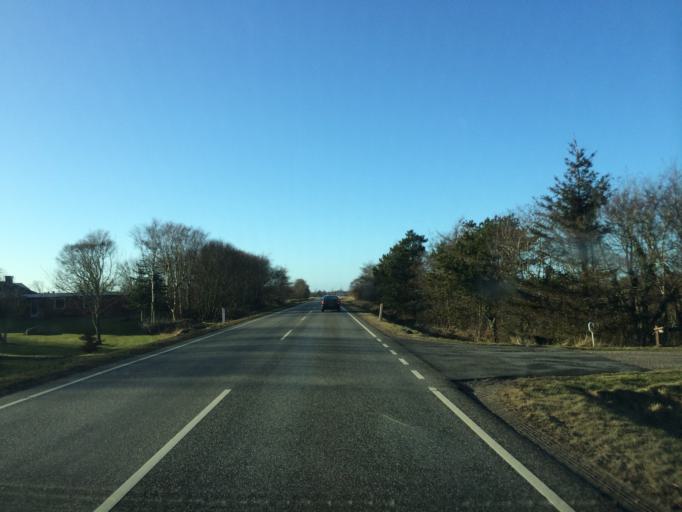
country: DK
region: Central Jutland
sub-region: Ringkobing-Skjern Kommune
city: Ringkobing
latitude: 56.1219
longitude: 8.2848
